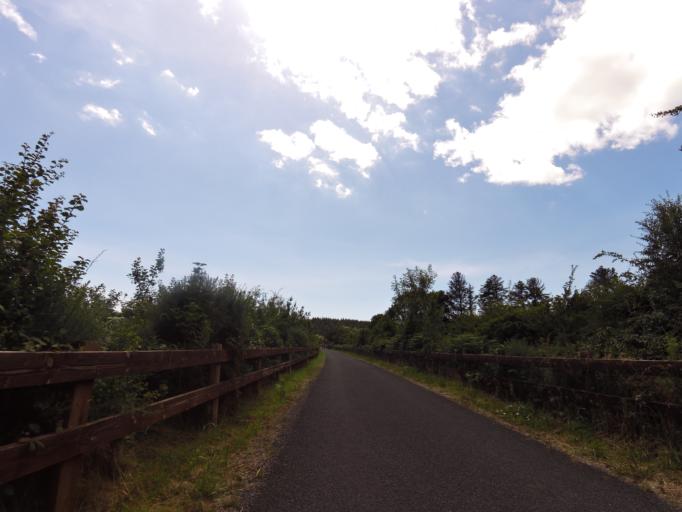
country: IE
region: Leinster
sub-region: Kilkenny
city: Mooncoin
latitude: 52.2424
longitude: -7.2642
